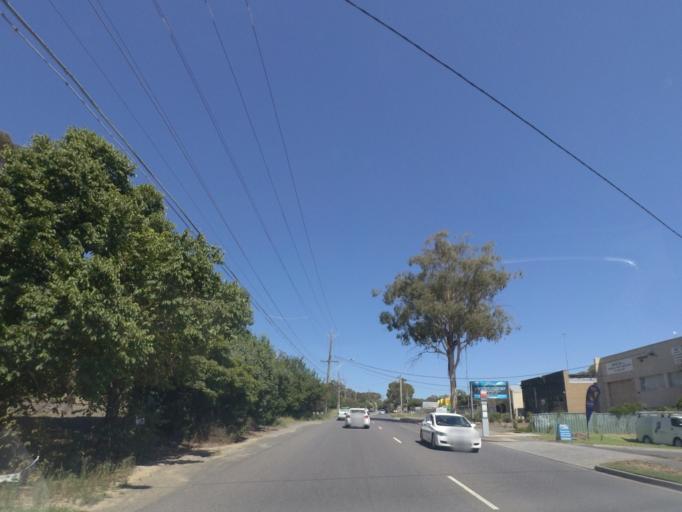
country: AU
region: Victoria
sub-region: Banyule
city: Greensborough
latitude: -37.7082
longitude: 145.1117
